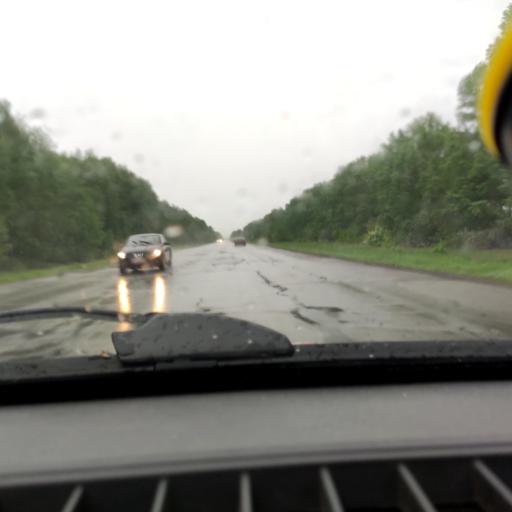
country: RU
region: Samara
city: Tol'yatti
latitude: 53.6419
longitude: 49.4205
